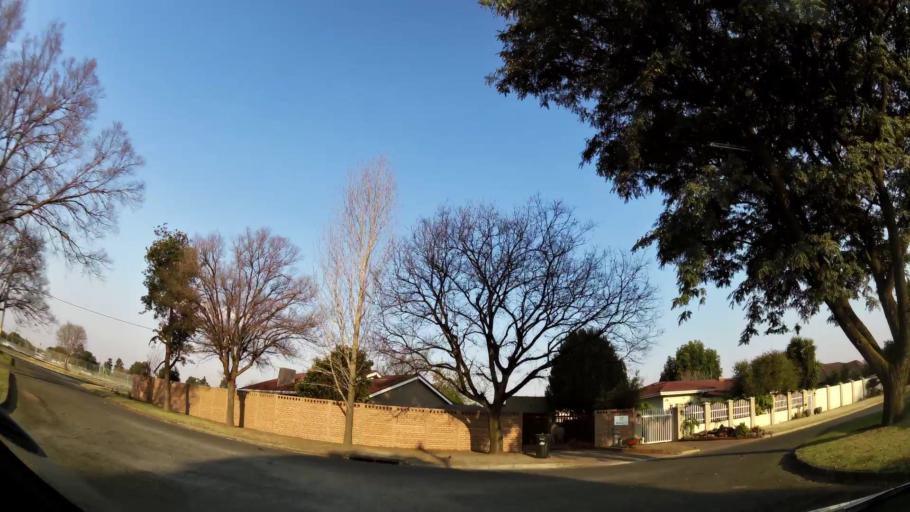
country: ZA
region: Gauteng
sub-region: Ekurhuleni Metropolitan Municipality
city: Springs
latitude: -26.2983
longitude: 28.4524
